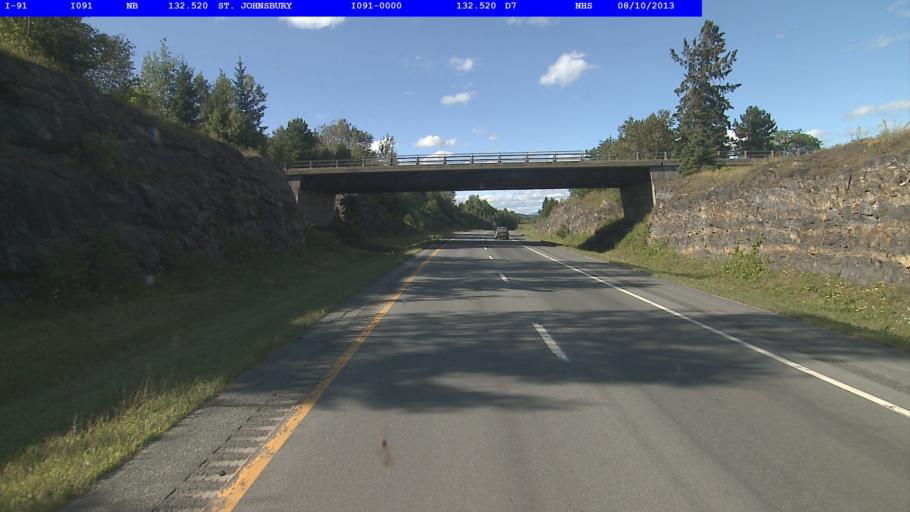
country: US
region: Vermont
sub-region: Caledonia County
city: St Johnsbury
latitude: 44.4533
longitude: -72.0243
